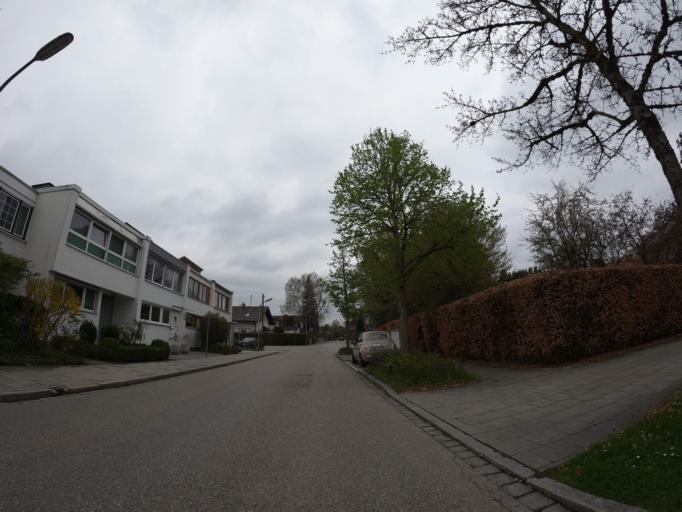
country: DE
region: Bavaria
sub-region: Upper Bavaria
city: Taufkirchen
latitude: 48.0417
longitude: 11.6269
